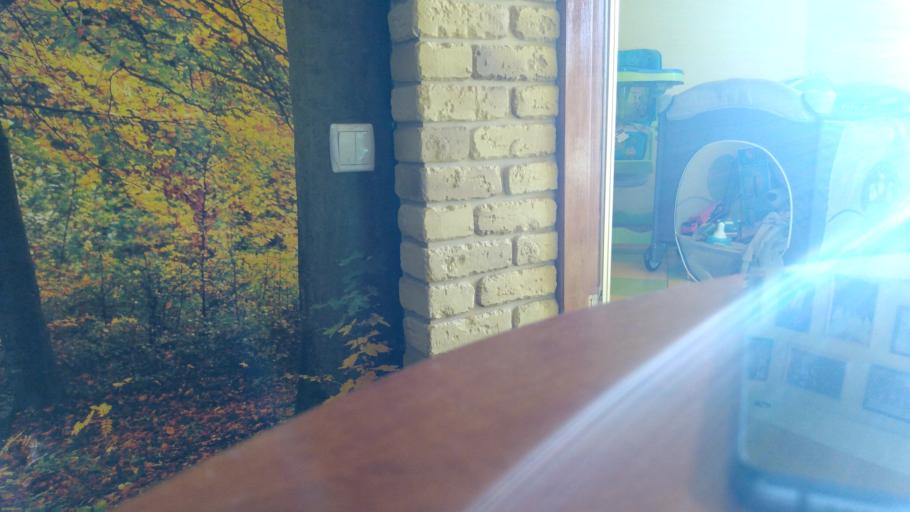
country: RU
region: Tverskaya
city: Likhoslavl'
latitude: 57.1486
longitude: 35.6112
